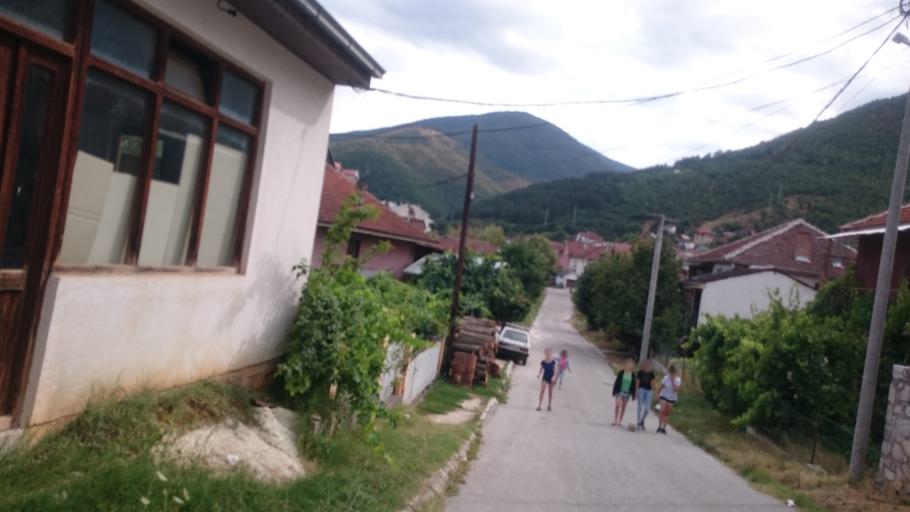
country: MK
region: Makedonski Brod
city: Makedonski Brod
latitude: 41.5154
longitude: 21.2166
